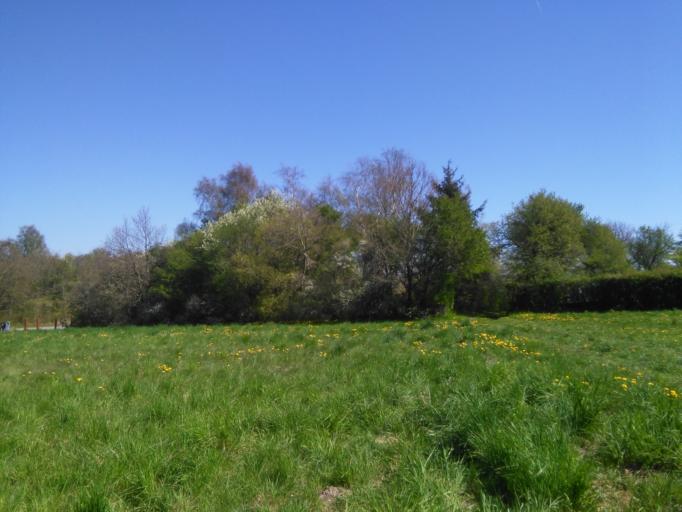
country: DK
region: Central Jutland
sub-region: Odder Kommune
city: Odder
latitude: 55.8788
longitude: 10.0562
